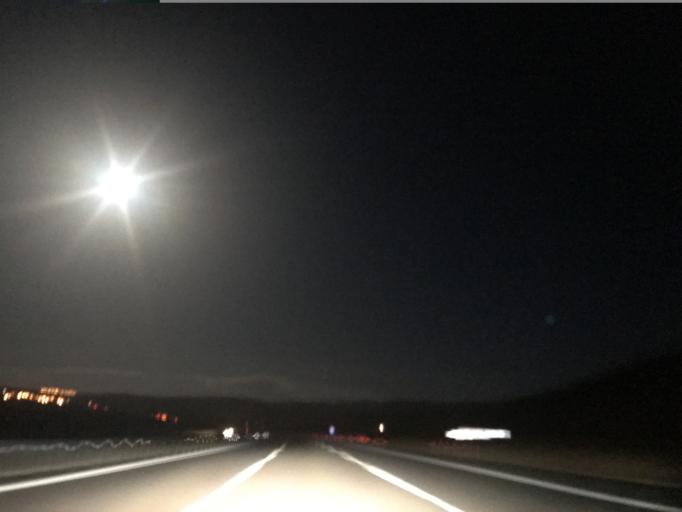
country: TR
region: Nigde
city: Ulukisla
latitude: 37.6318
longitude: 34.4544
